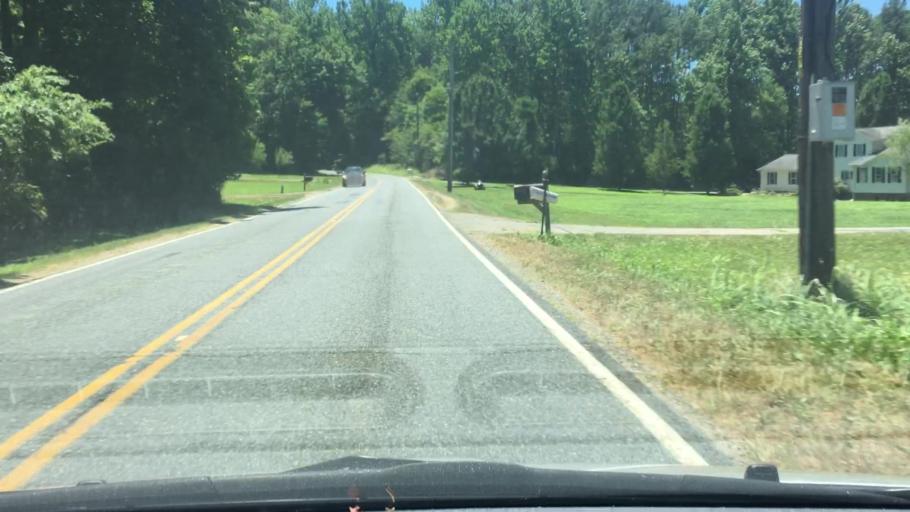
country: US
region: Maryland
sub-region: Saint Mary's County
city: Leonardtown
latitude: 38.3792
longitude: -76.5776
